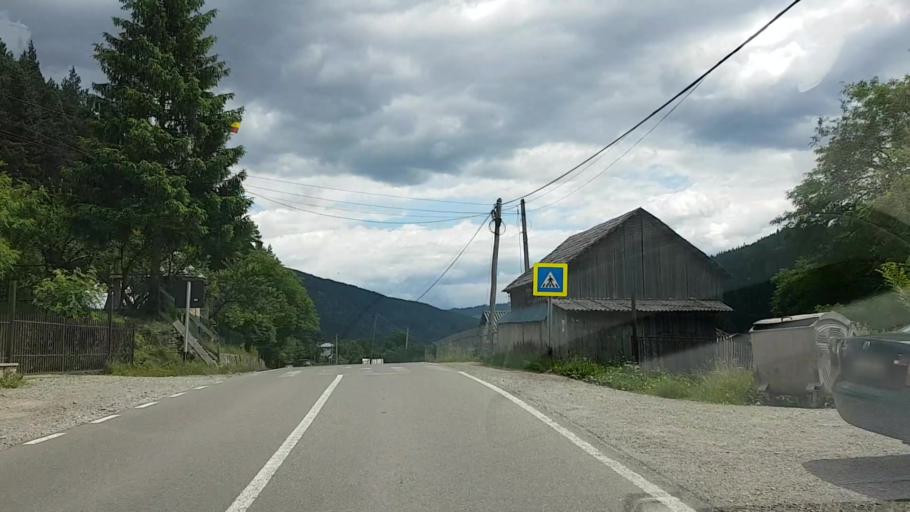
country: RO
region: Neamt
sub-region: Comuna Poiana Teiului
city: Poiana Teiului
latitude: 47.1202
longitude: 25.9125
